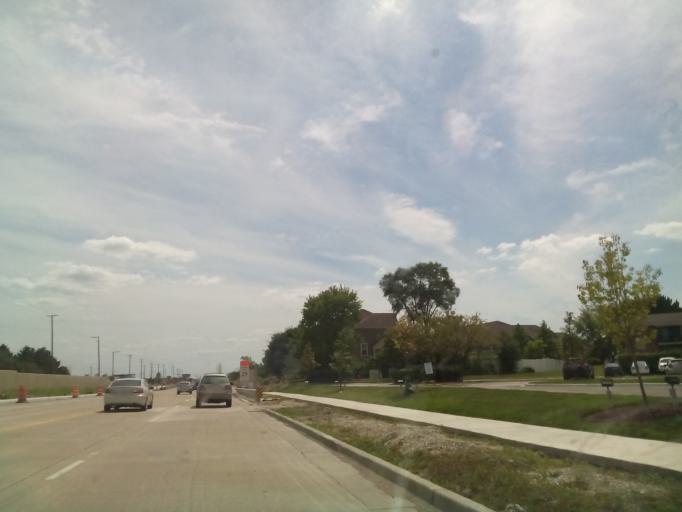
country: US
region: Illinois
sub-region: DuPage County
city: Warrenville
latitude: 41.7864
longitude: -88.2058
